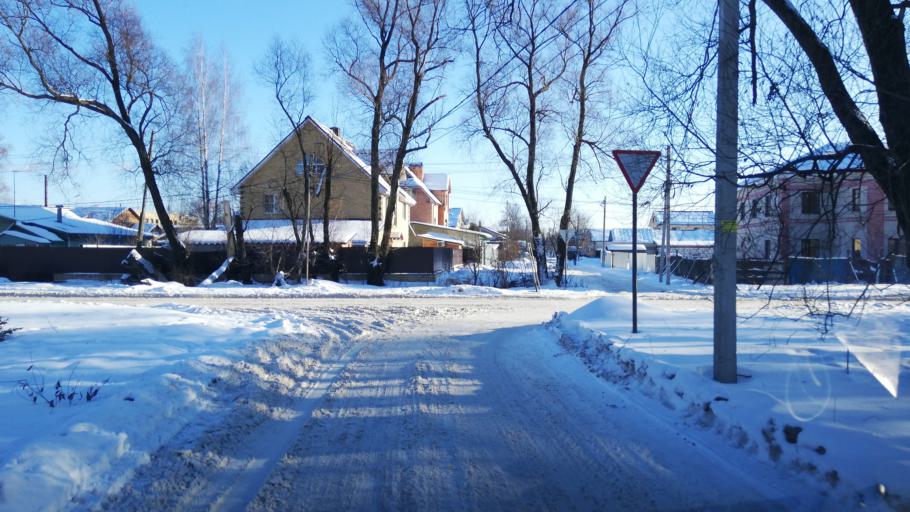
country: RU
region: Jaroslavl
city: Yaroslavl
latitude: 57.6099
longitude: 39.9005
